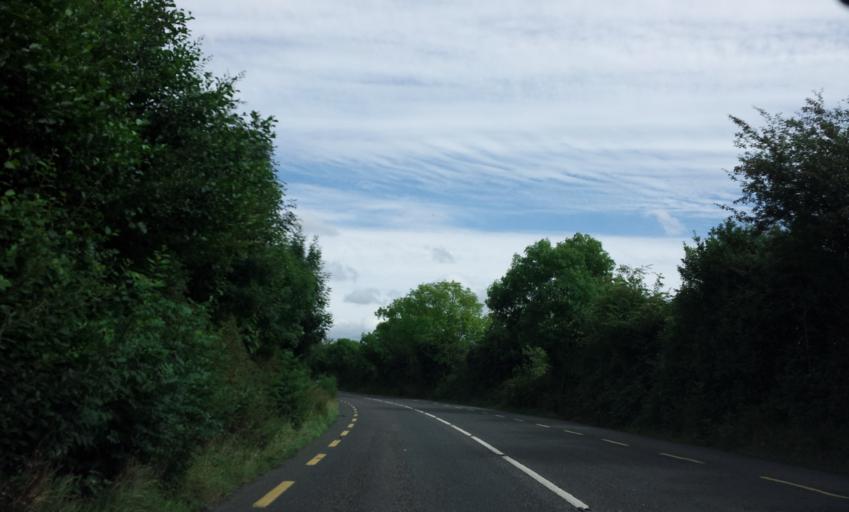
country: IE
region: Munster
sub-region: Ciarrai
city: Cill Airne
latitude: 52.0750
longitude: -9.6444
